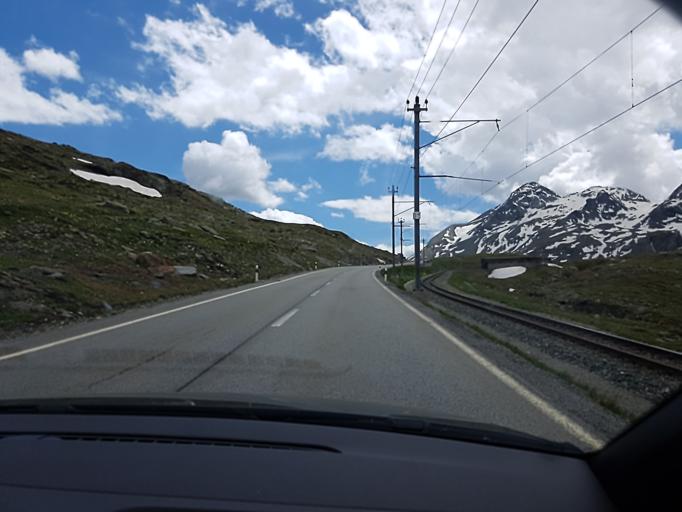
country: CH
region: Grisons
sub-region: Bernina District
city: Poschiavo
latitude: 46.4236
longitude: 10.0014
